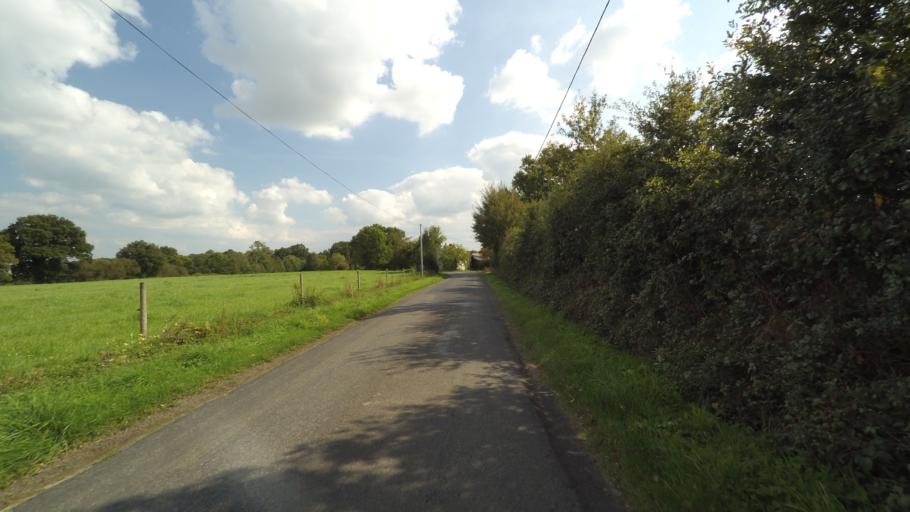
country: FR
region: Pays de la Loire
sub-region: Departement de la Vendee
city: Bouffere
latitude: 46.9536
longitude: -1.3750
